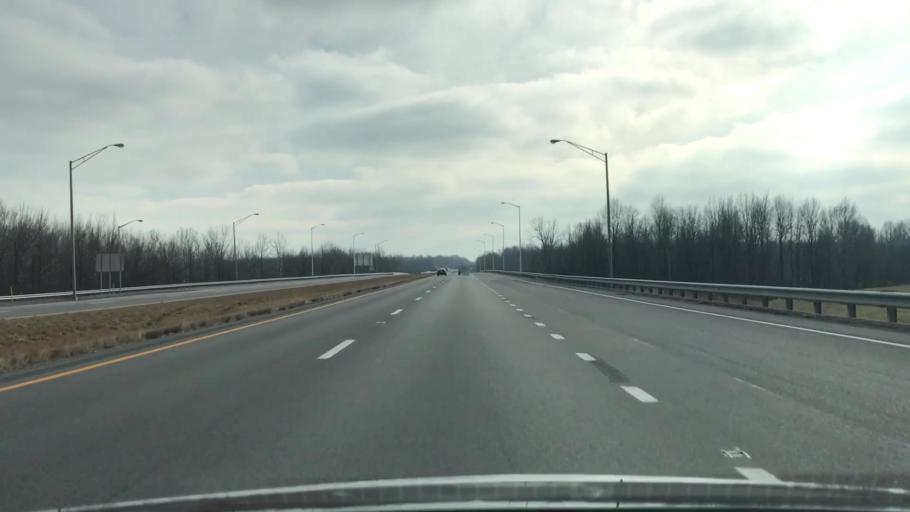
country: US
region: Kentucky
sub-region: Hopkins County
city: Madisonville
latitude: 37.2941
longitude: -87.4620
